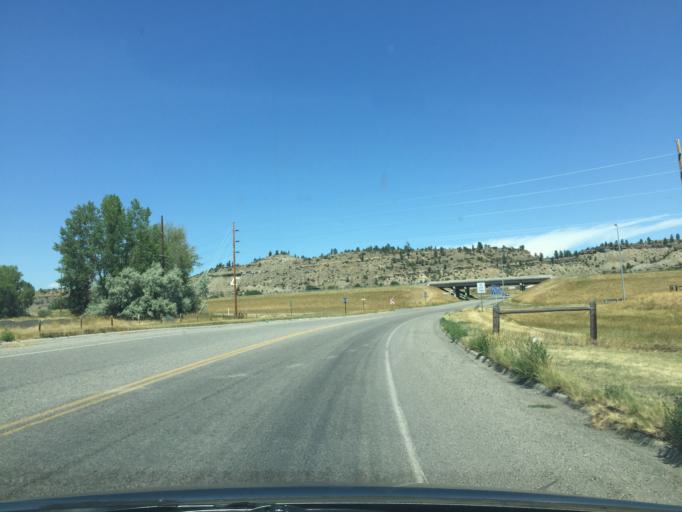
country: US
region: Montana
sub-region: Stillwater County
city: Columbus
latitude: 45.6448
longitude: -109.2487
